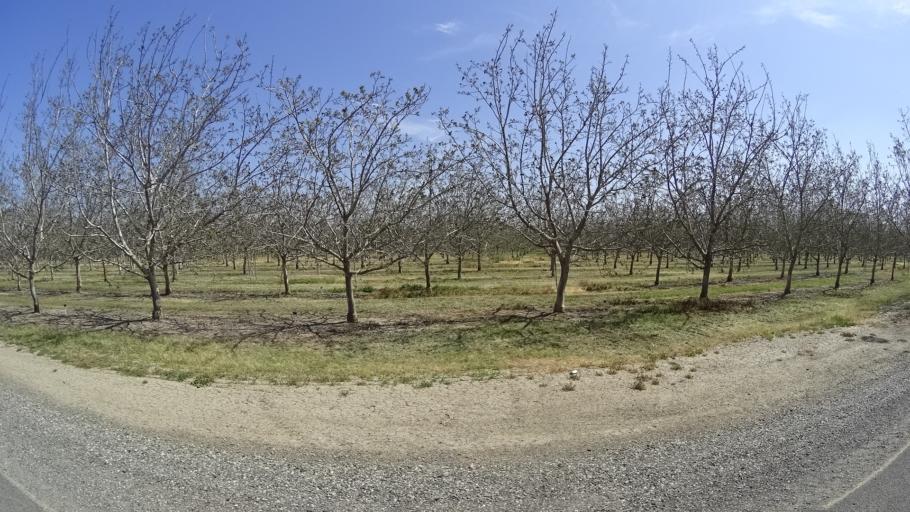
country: US
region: California
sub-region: Glenn County
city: Willows
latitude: 39.5097
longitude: -122.0173
